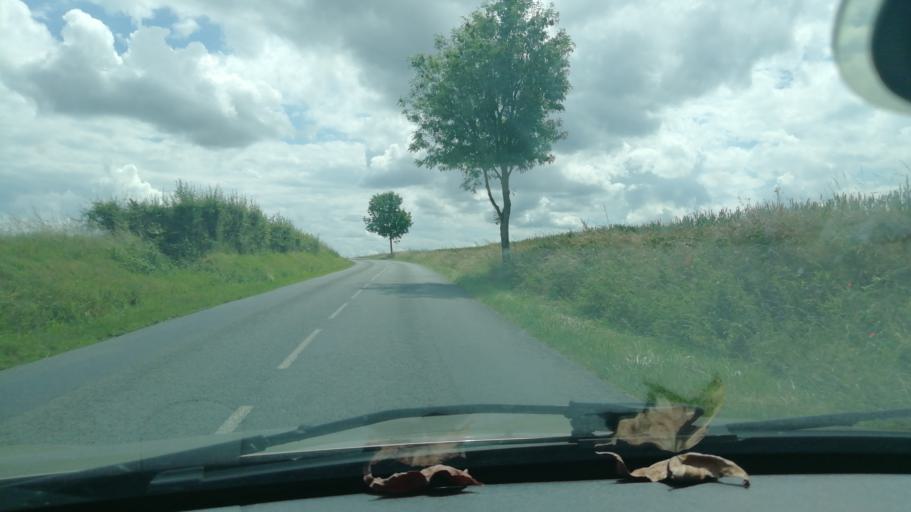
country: FR
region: Nord-Pas-de-Calais
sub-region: Departement du Pas-de-Calais
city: Aubigny-en-Artois
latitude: 50.3374
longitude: 2.5892
